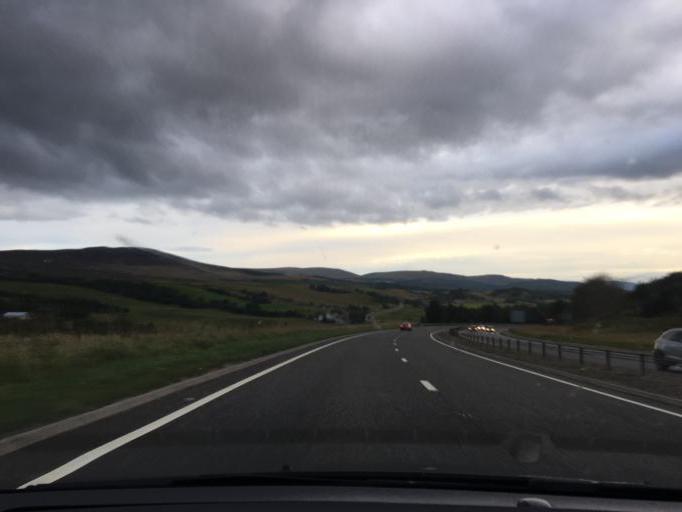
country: GB
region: Scotland
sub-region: Highland
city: Inverness
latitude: 57.4280
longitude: -4.1259
